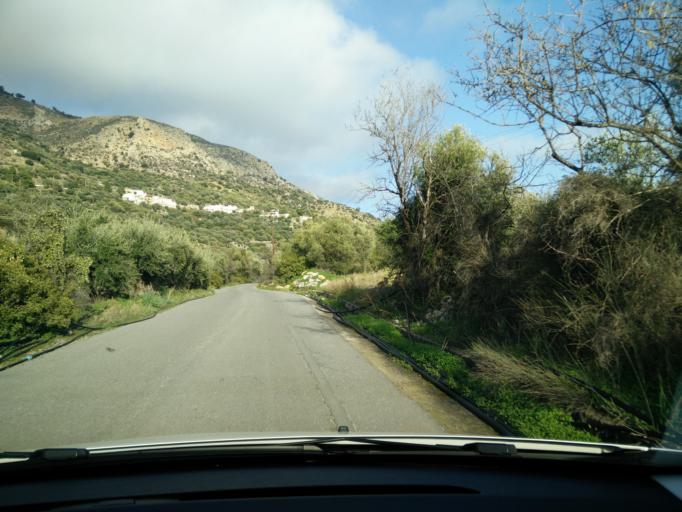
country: GR
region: Crete
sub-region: Nomos Lasithiou
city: Gra Liyia
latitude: 35.0247
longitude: 25.5449
